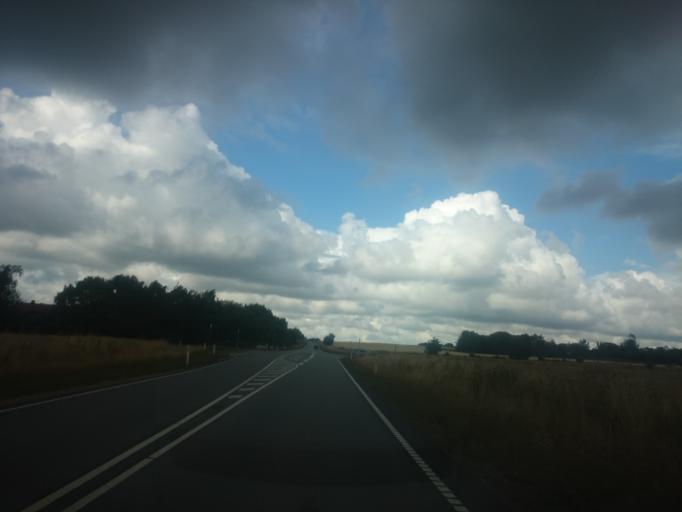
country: DK
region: South Denmark
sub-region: Billund Kommune
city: Grindsted
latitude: 55.6963
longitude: 8.9740
